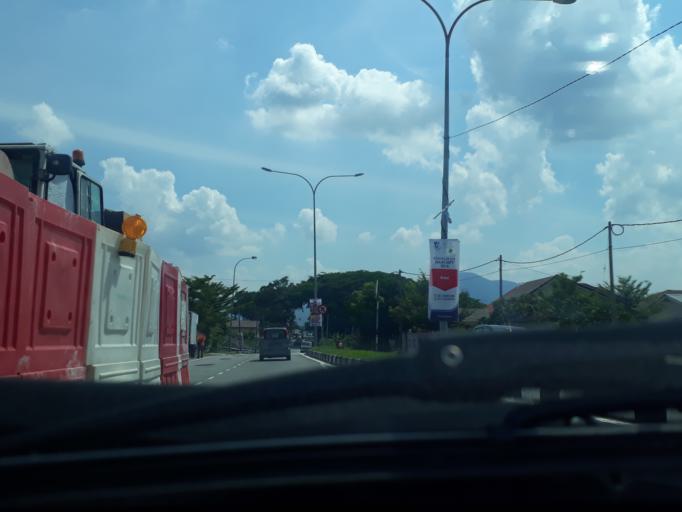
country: MY
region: Perak
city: Ipoh
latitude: 4.5774
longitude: 101.0897
